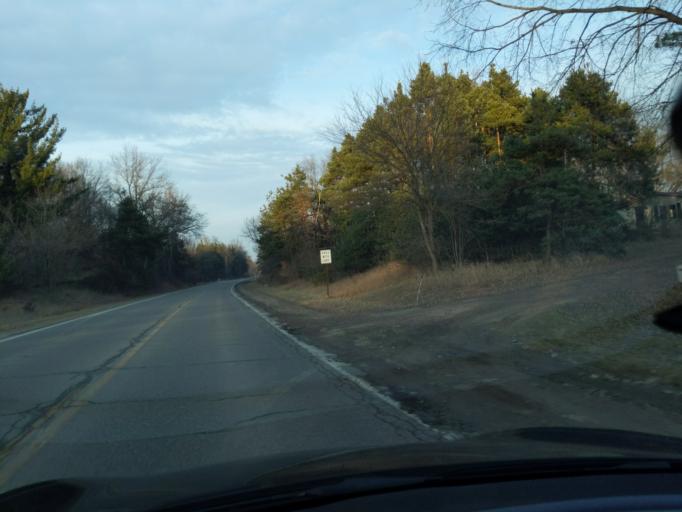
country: US
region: Michigan
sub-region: Livingston County
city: Brighton
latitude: 42.5959
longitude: -83.7532
